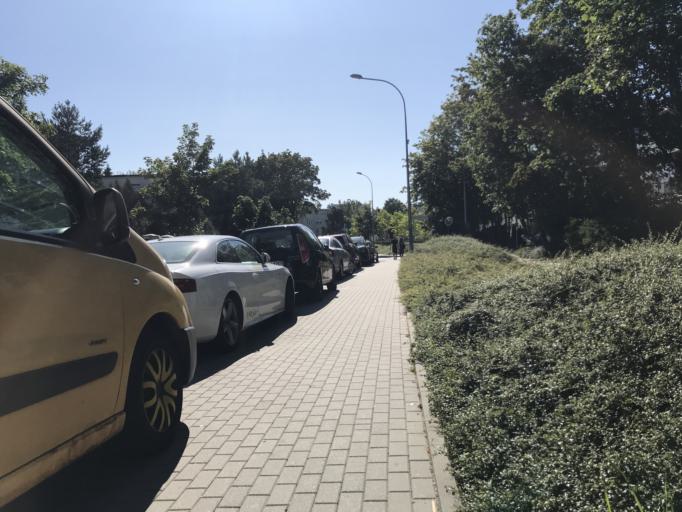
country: PL
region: Pomeranian Voivodeship
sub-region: Sopot
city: Sopot
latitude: 54.4798
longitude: 18.5551
